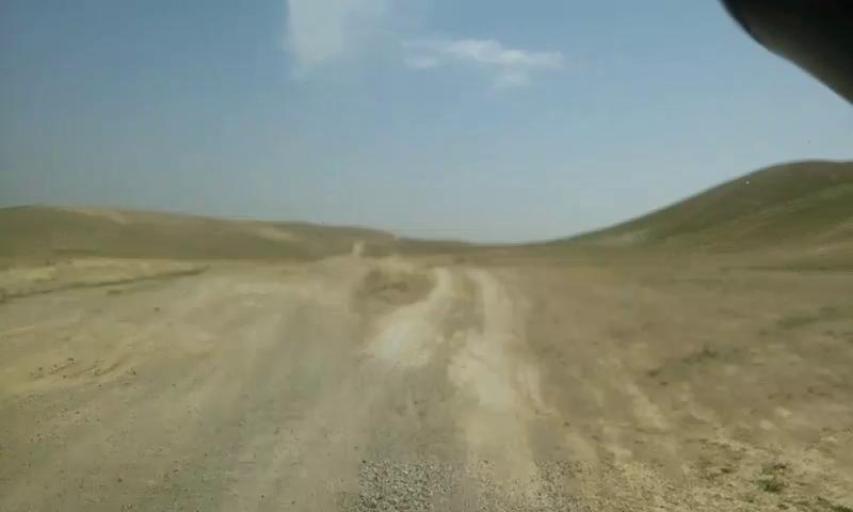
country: PS
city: `Arab ar Rashaydah
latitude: 31.5295
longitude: 35.2890
